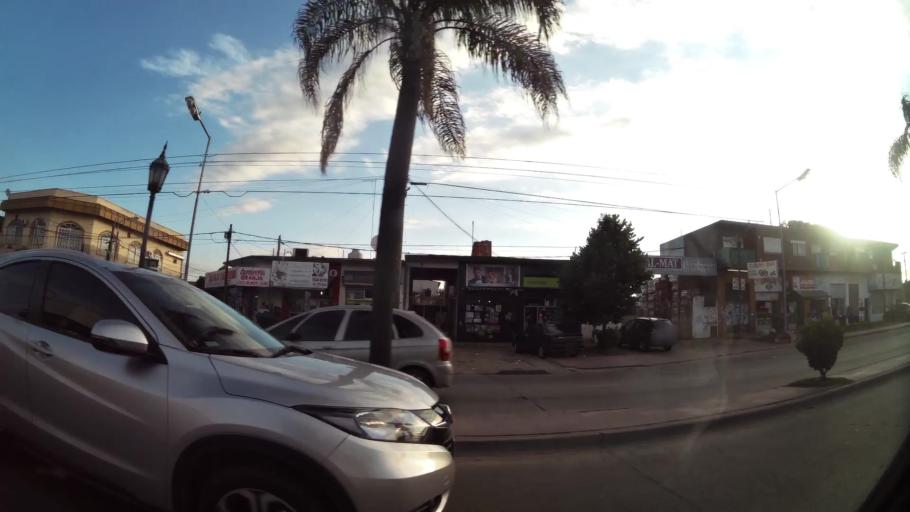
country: AR
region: Buenos Aires
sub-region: Partido de Tigre
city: Tigre
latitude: -34.4533
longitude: -58.6512
